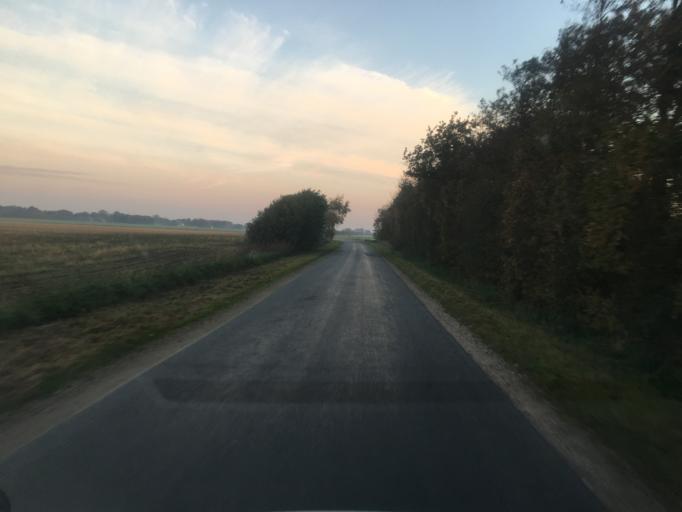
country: DK
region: South Denmark
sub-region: Tonder Kommune
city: Logumkloster
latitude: 54.9917
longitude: 9.0507
